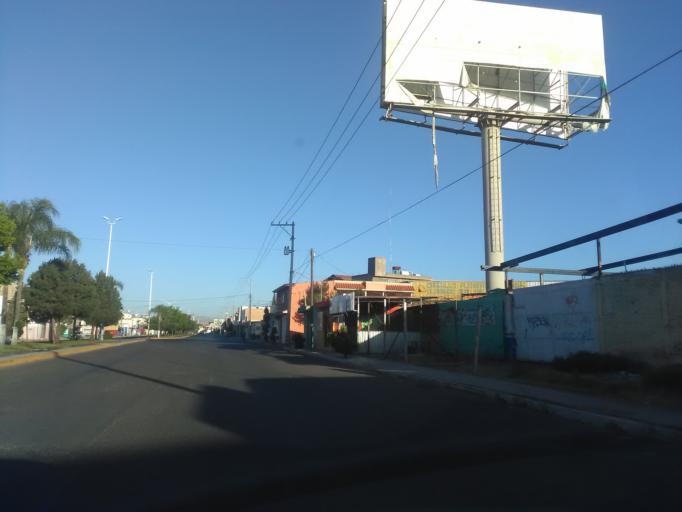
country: MX
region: Durango
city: Victoria de Durango
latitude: 24.0163
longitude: -104.6472
